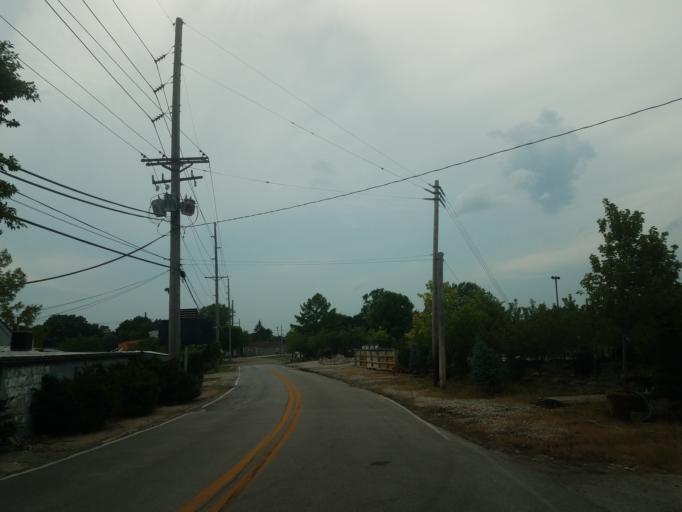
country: US
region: Illinois
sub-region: McLean County
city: Bloomington
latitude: 40.4632
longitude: -88.9915
